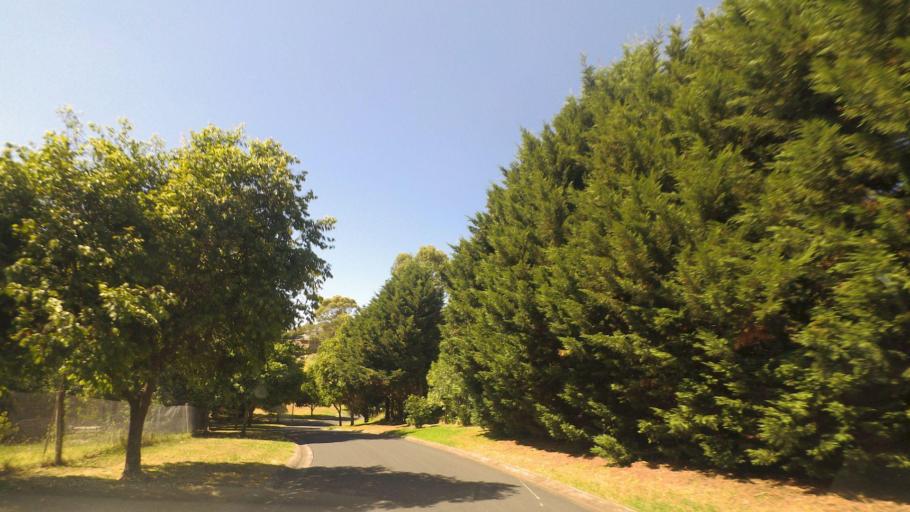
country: AU
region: Victoria
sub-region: Manningham
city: Park Orchards
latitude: -37.7709
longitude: 145.2273
